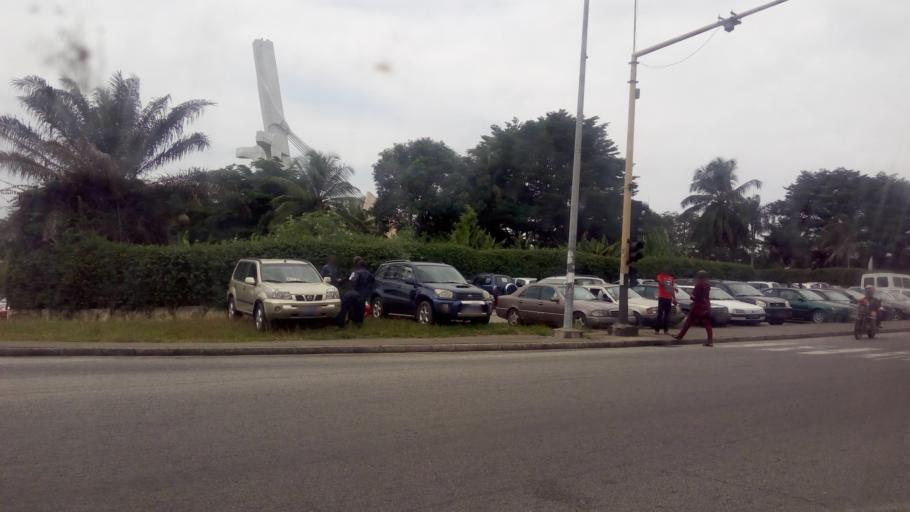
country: CI
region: Lagunes
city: Abidjan
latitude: 5.3344
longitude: -4.0217
